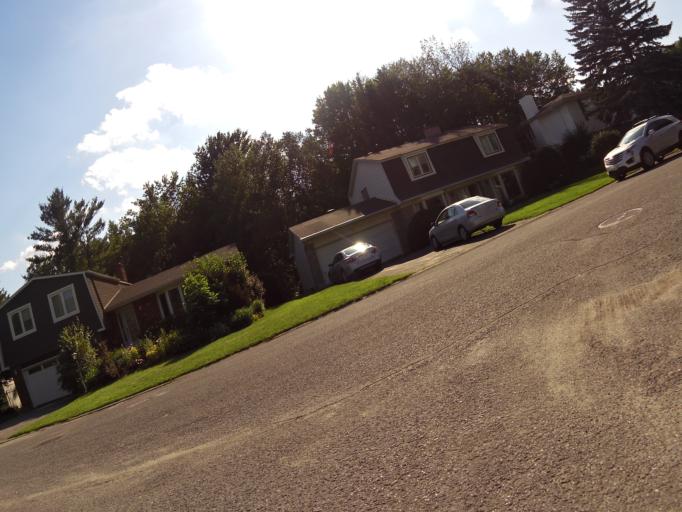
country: CA
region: Ontario
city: Bells Corners
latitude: 45.3202
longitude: -75.7893
